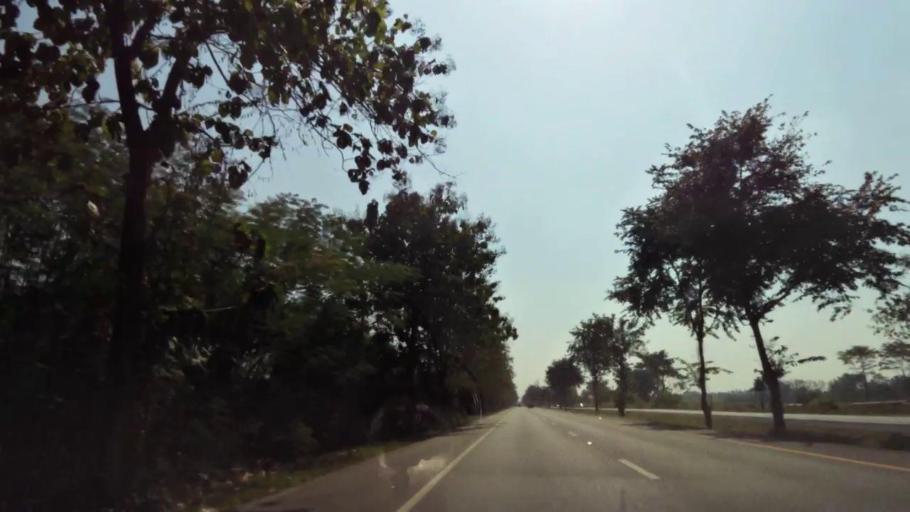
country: TH
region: Phichit
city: Bueng Na Rang
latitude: 16.0875
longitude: 100.1249
